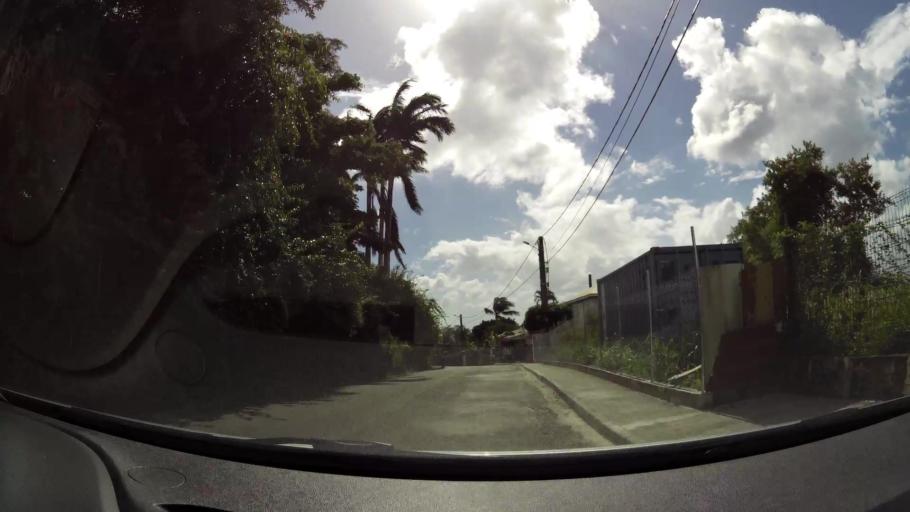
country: MQ
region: Martinique
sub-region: Martinique
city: Fort-de-France
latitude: 14.6014
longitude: -61.0891
